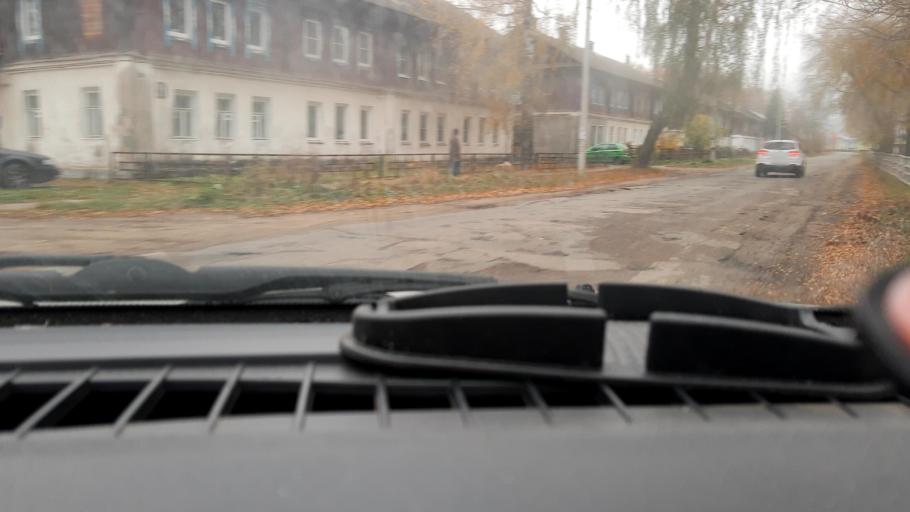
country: RU
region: Nizjnij Novgorod
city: Neklyudovo
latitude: 56.4084
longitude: 44.0320
